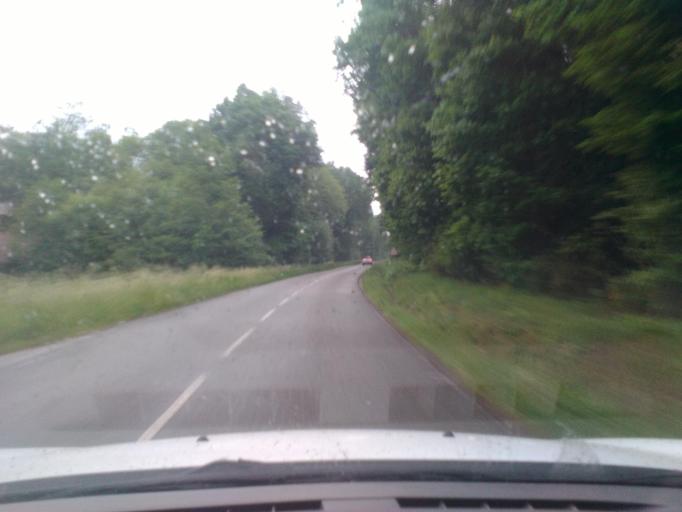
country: FR
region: Lorraine
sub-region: Departement des Vosges
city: Jeanmenil
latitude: 48.2748
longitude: 6.7140
